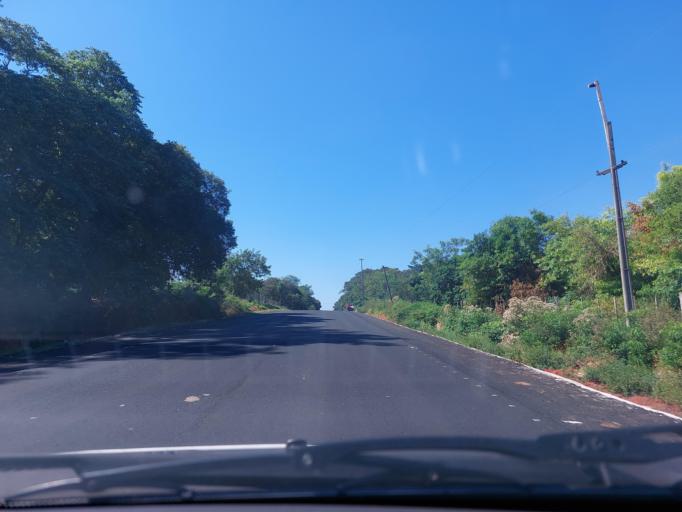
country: PY
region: San Pedro
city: Guayaybi
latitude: -24.5503
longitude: -56.4994
